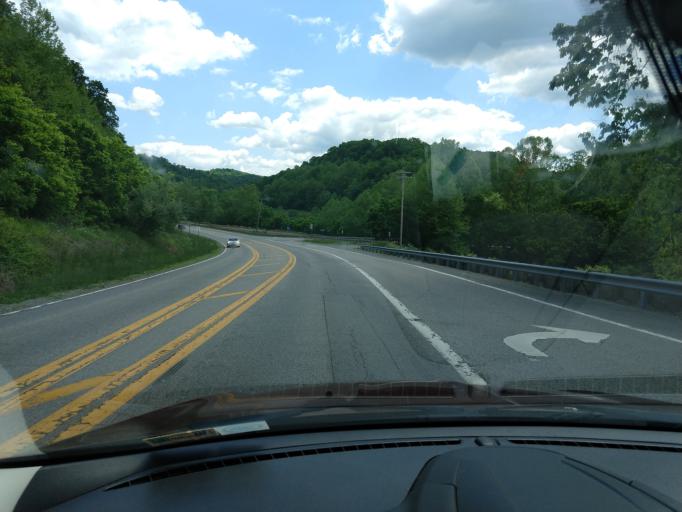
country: US
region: West Virginia
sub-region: Gilmer County
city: Glenville
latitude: 38.9295
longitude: -80.7850
